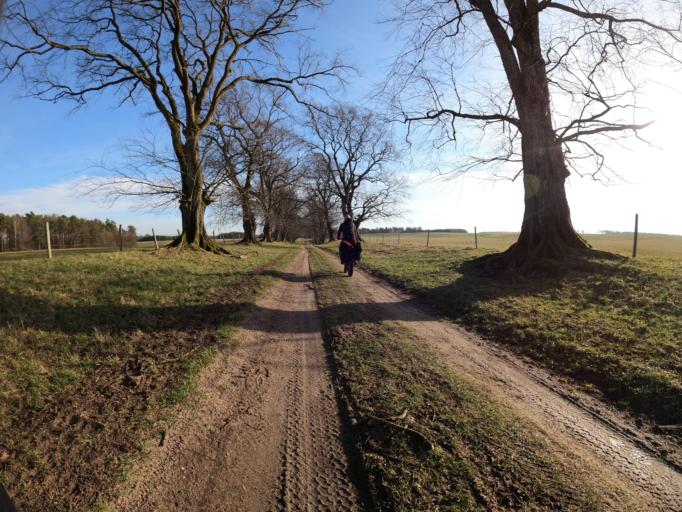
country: PL
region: West Pomeranian Voivodeship
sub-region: Powiat koszalinski
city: Polanow
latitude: 54.1973
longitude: 16.6568
